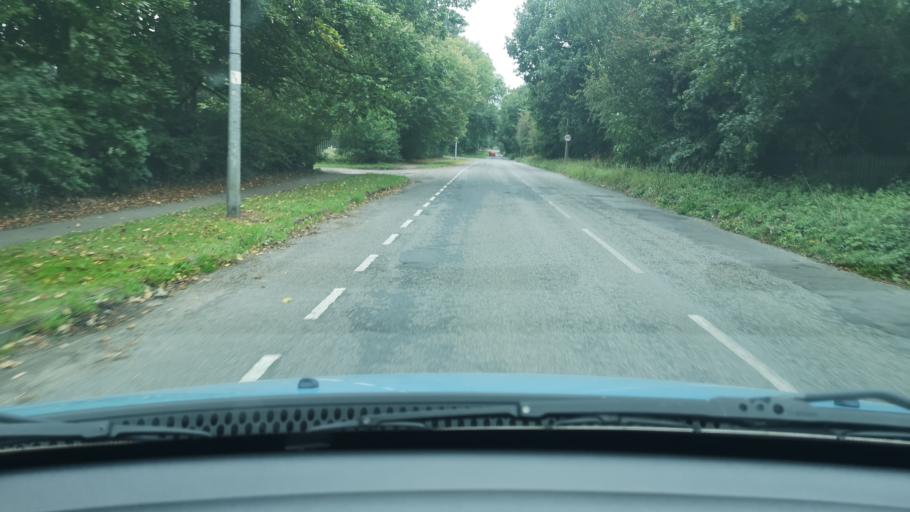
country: GB
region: England
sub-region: North Lincolnshire
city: Scunthorpe
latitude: 53.5844
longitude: -0.6775
